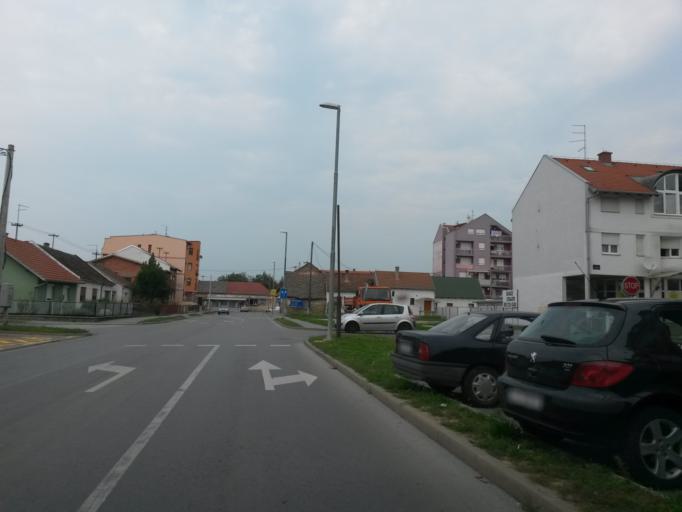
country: HR
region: Osjecko-Baranjska
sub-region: Grad Osijek
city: Osijek
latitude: 45.5495
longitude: 18.7093
